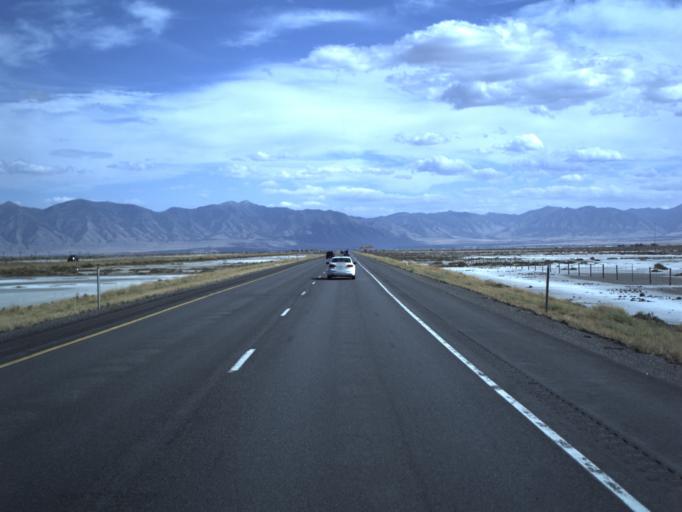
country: US
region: Utah
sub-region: Tooele County
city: Grantsville
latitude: 40.6988
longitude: -112.4840
